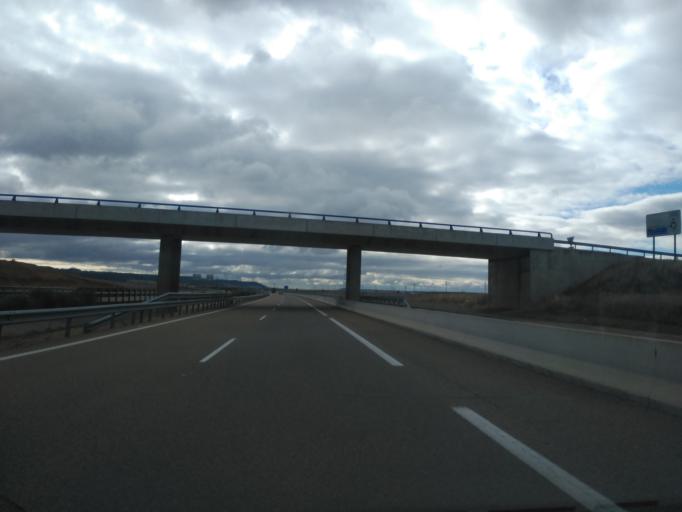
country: ES
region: Castille and Leon
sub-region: Provincia de Palencia
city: Fuentes de Valdepero
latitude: 42.0714
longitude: -4.4924
